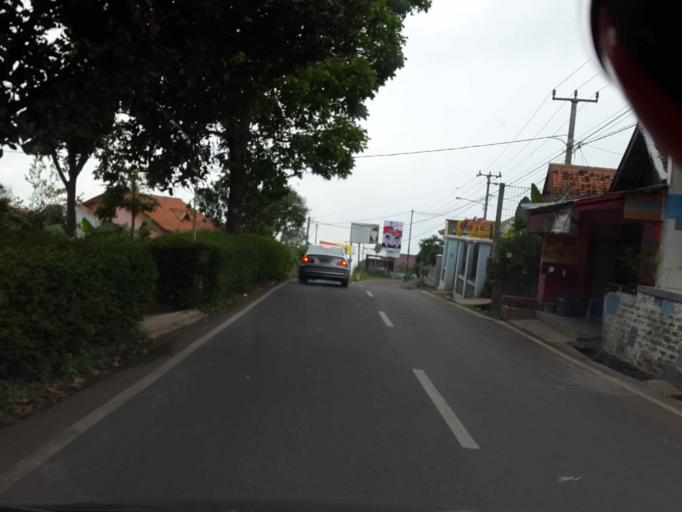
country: ID
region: West Java
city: Cimahi
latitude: -6.8167
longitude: 107.5457
